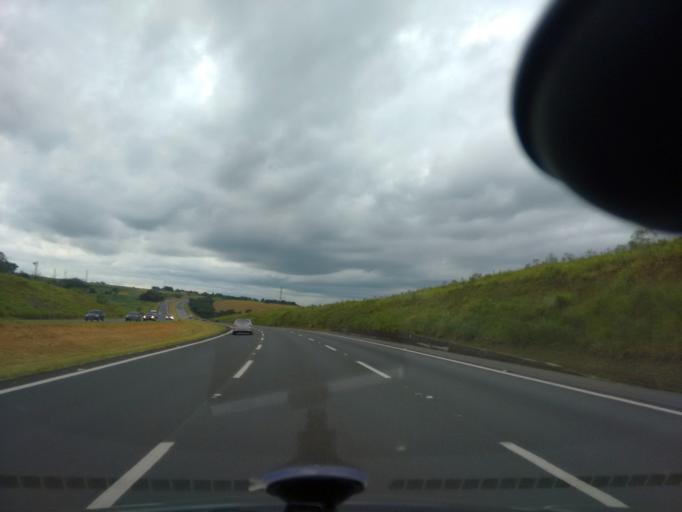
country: BR
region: Sao Paulo
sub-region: Hortolandia
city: Hortolandia
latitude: -22.8834
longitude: -47.2333
